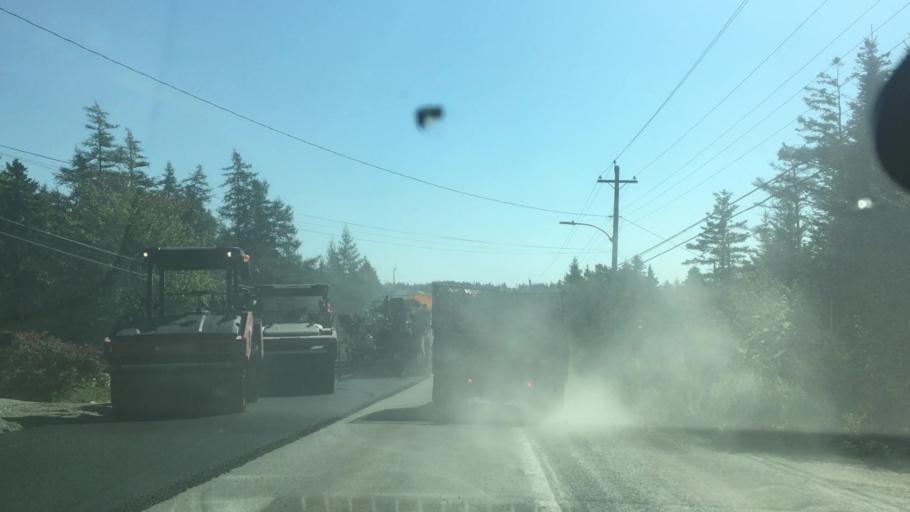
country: CA
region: Nova Scotia
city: New Glasgow
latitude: 44.9079
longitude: -62.4981
